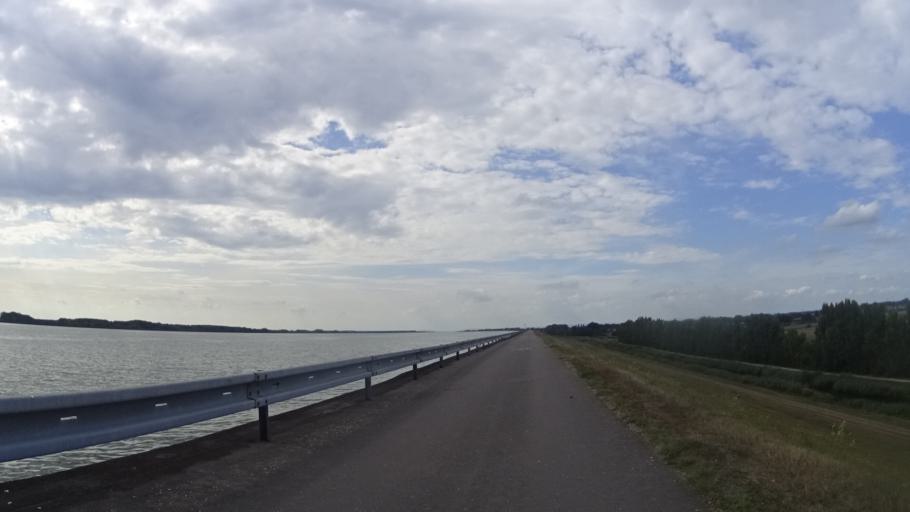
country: SK
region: Trnavsky
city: Gabcikovo
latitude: 47.8924
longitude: 17.5309
